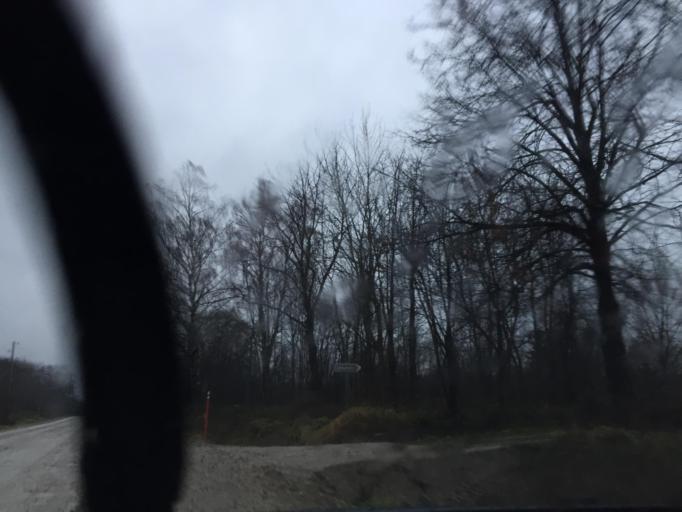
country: LV
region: Salacgrivas
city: Salacgriva
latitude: 57.7637
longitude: 24.4638
